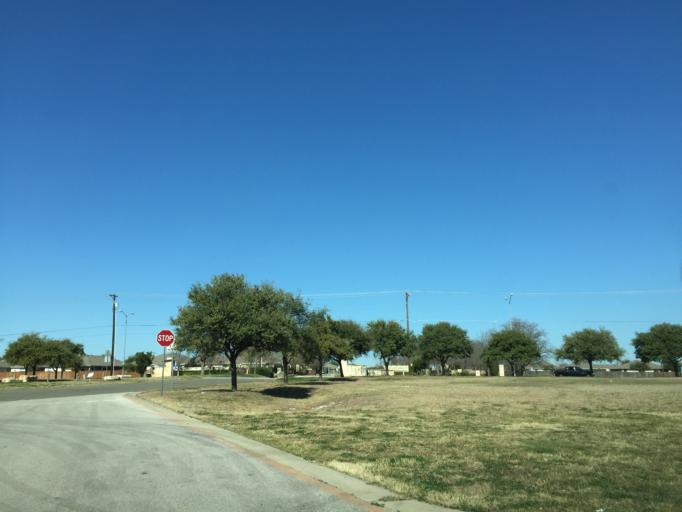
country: US
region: Texas
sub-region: Williamson County
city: Hutto
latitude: 30.5457
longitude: -97.6176
